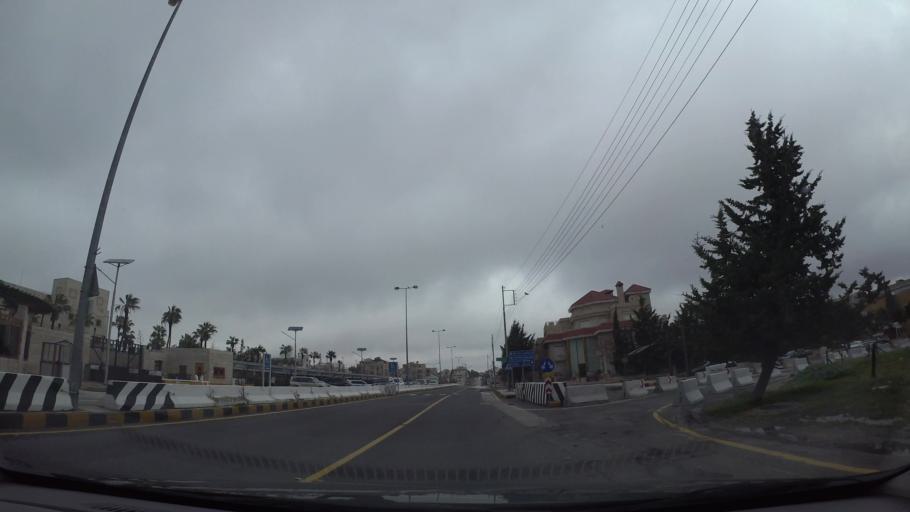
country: JO
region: Amman
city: Al Bunayyat ash Shamaliyah
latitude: 31.9448
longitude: 35.8815
